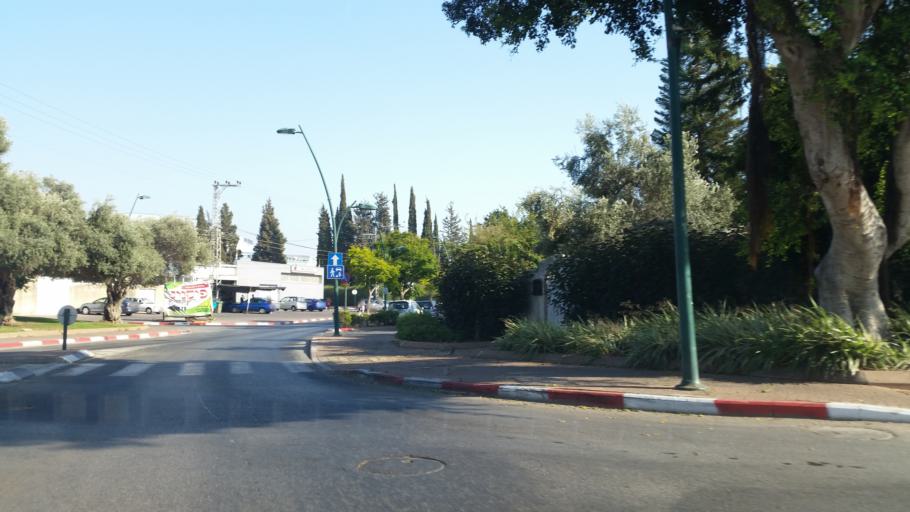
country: IL
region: Tel Aviv
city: Ramat HaSharon
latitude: 32.1292
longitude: 34.8559
